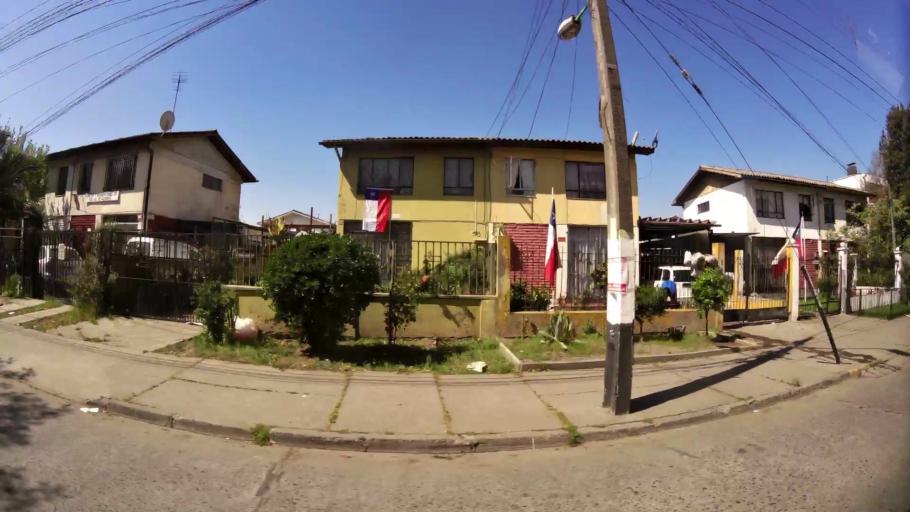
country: CL
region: Santiago Metropolitan
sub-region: Provincia de Santiago
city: Lo Prado
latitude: -33.5092
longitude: -70.7344
